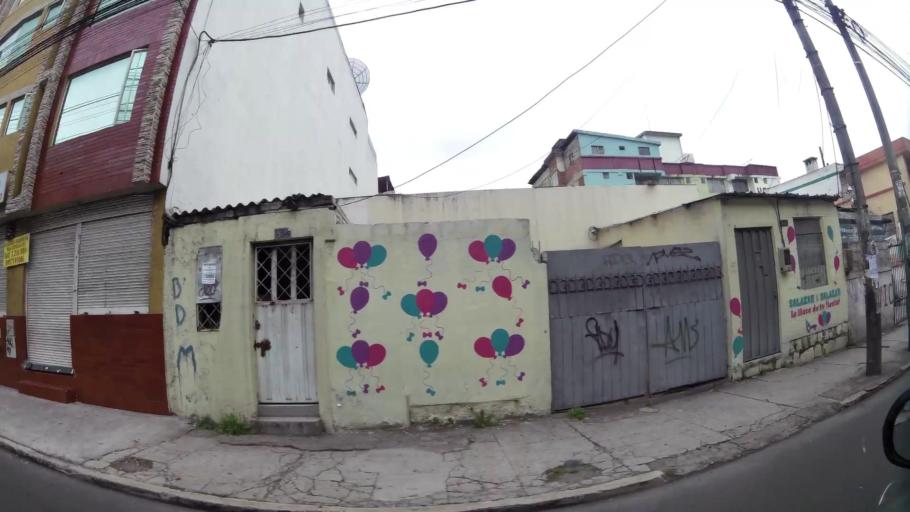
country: EC
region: Pichincha
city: Quito
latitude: -0.1982
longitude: -78.4984
